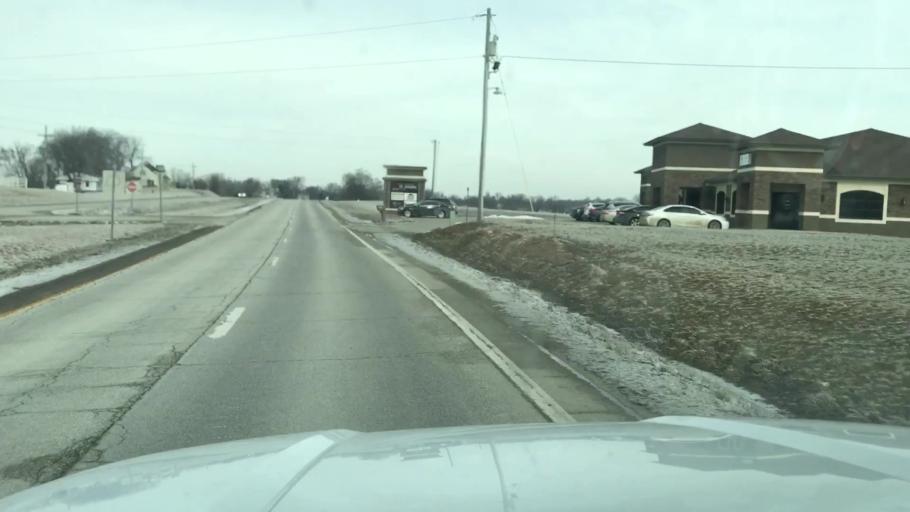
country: US
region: Missouri
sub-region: Andrew County
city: Country Club Village
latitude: 39.8864
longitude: -94.8086
